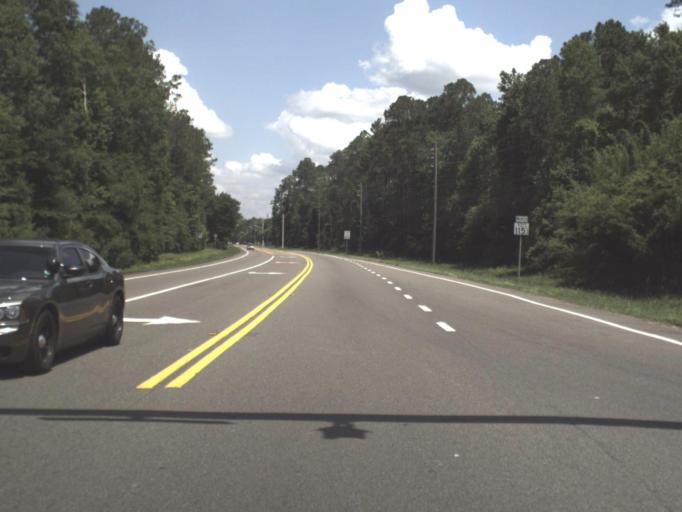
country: US
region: Florida
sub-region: Nassau County
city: Nassau Village-Ratliff
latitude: 30.4749
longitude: -81.7119
